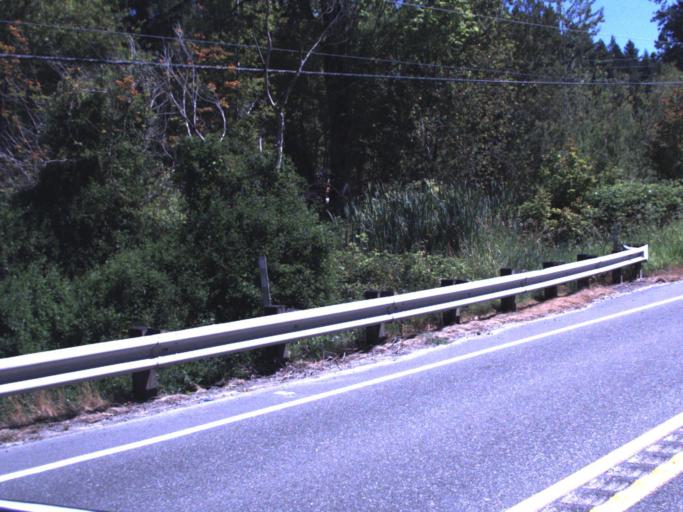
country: US
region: Washington
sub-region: King County
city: Fall City
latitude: 47.5616
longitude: -121.8624
